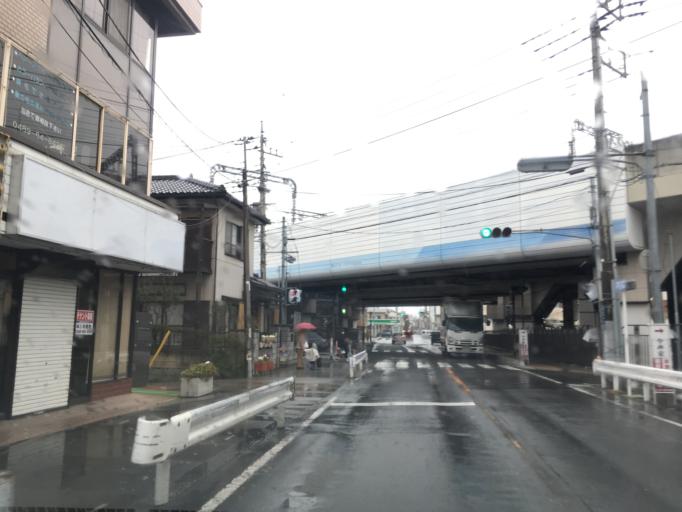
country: JP
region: Saitama
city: Koshigaya
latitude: 35.8893
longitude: 139.7853
